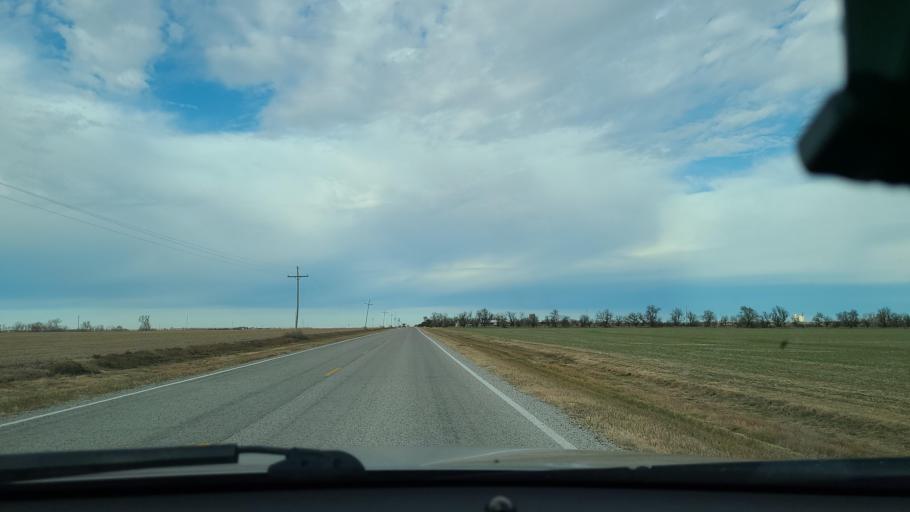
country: US
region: Kansas
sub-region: McPherson County
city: Inman
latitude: 38.3628
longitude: -97.9244
